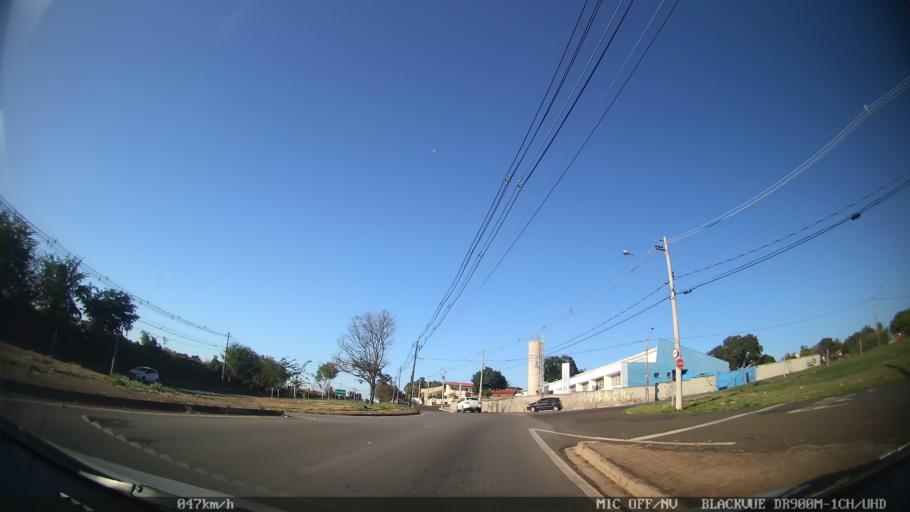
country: BR
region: Sao Paulo
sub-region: Nova Odessa
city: Nova Odessa
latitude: -22.7718
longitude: -47.2811
